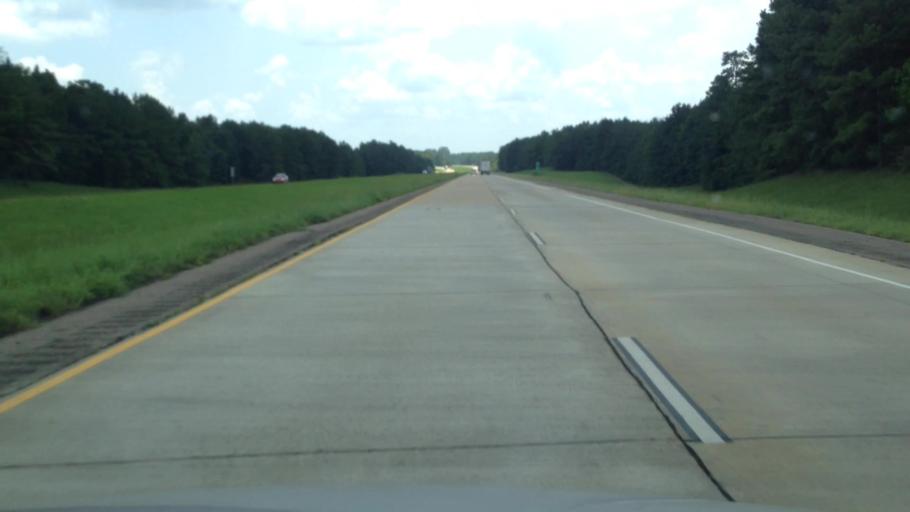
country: US
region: Louisiana
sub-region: Rapides Parish
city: Lecompte
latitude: 31.0491
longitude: -92.4211
